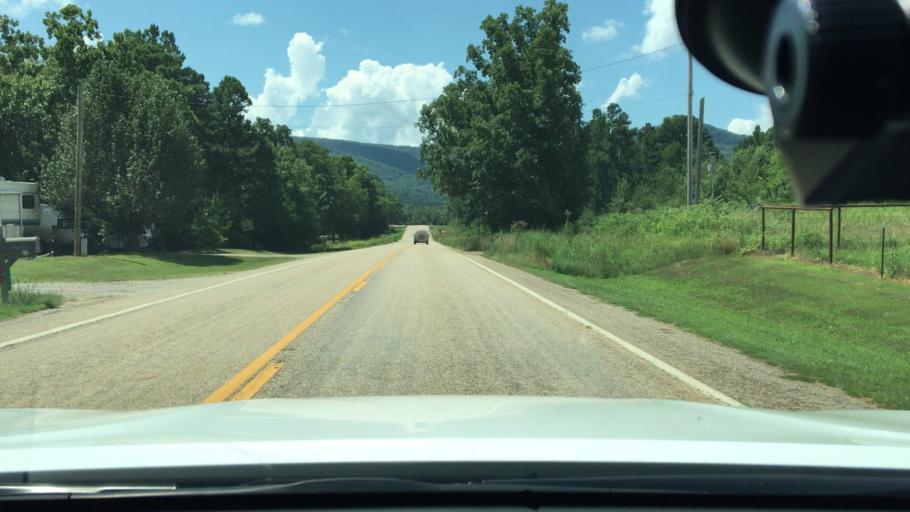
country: US
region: Arkansas
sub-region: Logan County
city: Paris
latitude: 35.2025
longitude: -93.6348
